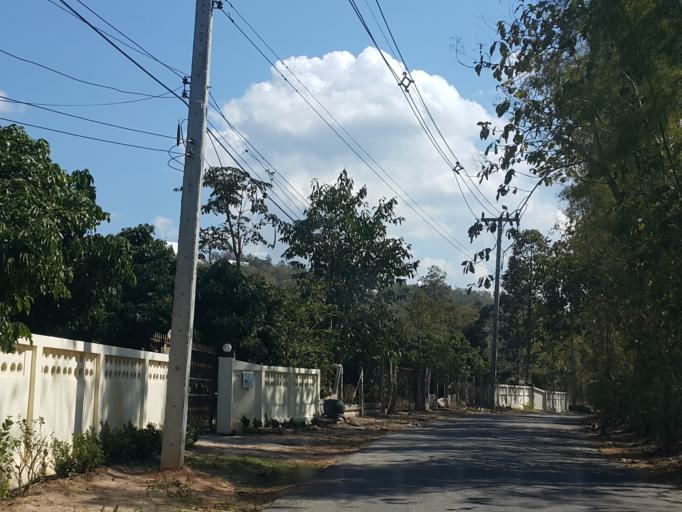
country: TH
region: Chiang Mai
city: Mae Taeng
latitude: 19.0358
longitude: 98.9882
